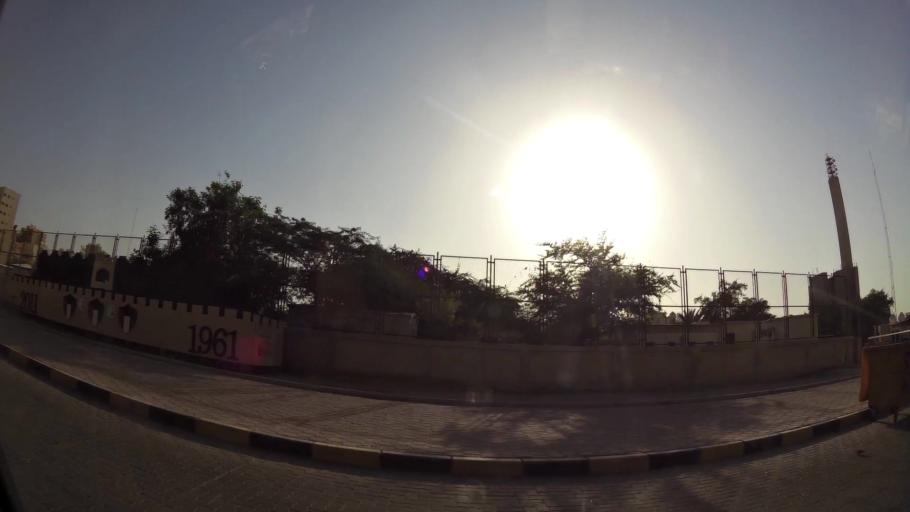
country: KW
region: Muhafazat Hawalli
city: As Salimiyah
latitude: 29.3379
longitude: 48.0860
